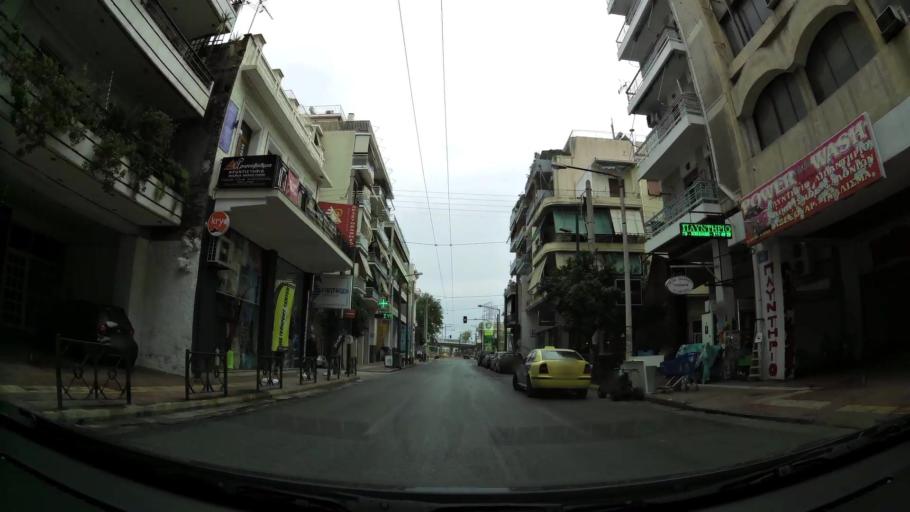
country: GR
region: Attica
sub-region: Nomarchia Athinas
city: Moskhaton
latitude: 37.9440
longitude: 23.6607
